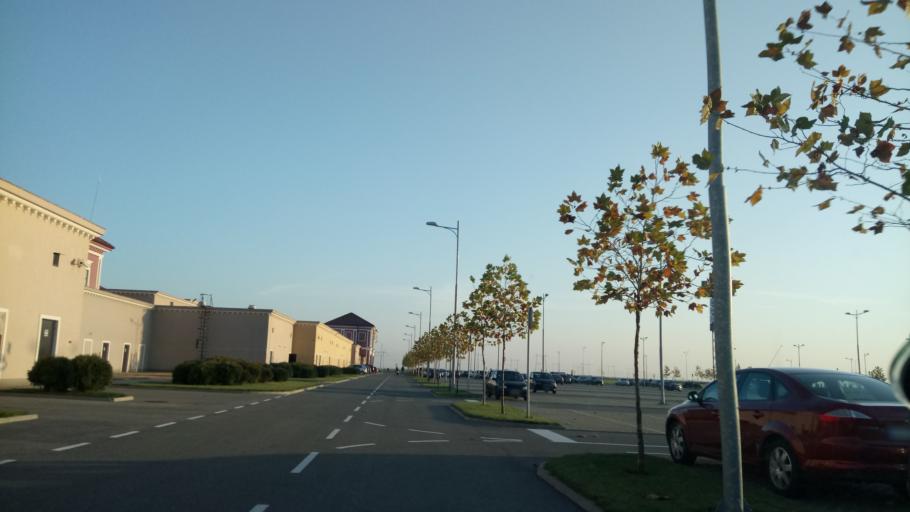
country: RS
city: Novi Karlovci
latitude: 45.0696
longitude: 20.1359
